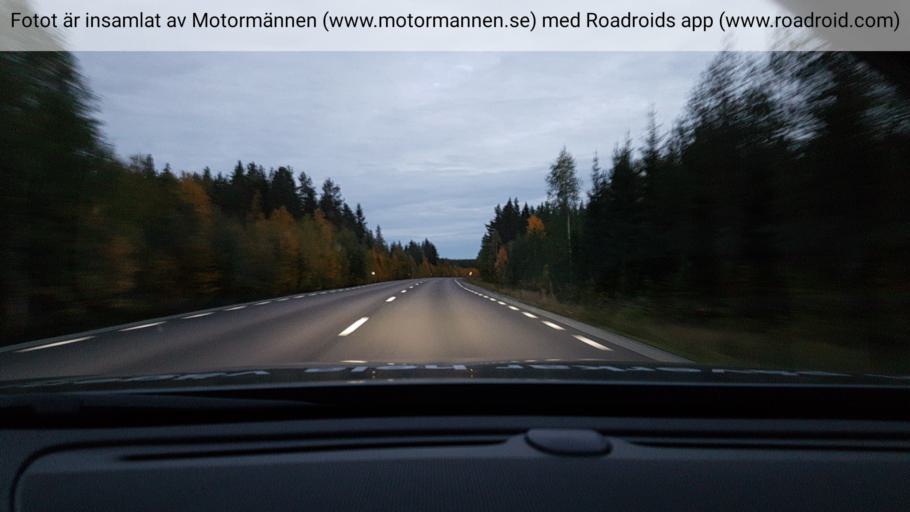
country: SE
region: Norrbotten
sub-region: Alvsbyns Kommun
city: AElvsbyn
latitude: 65.7309
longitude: 20.9821
